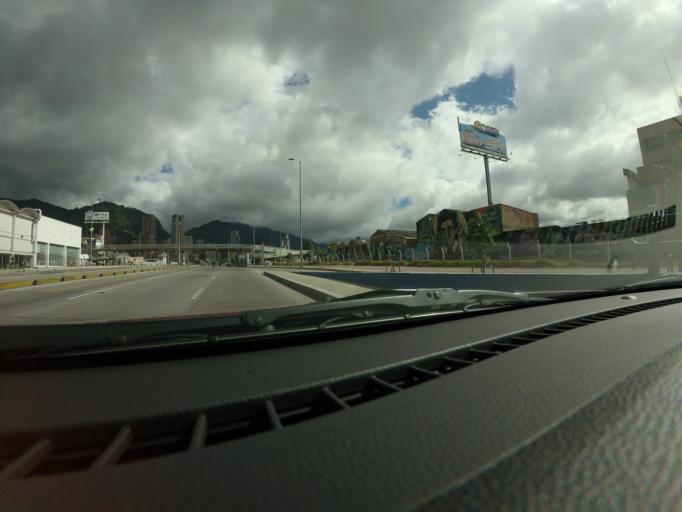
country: CO
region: Bogota D.C.
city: Bogota
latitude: 4.6212
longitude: -74.0777
